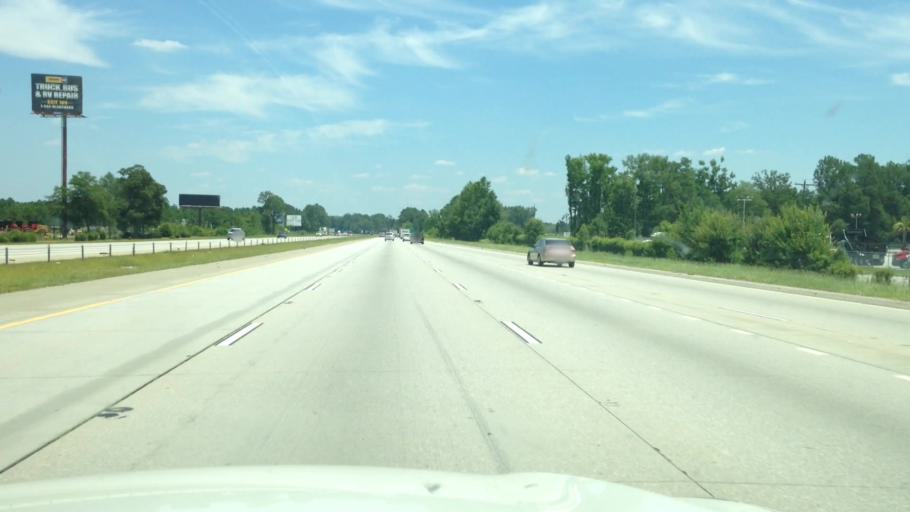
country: US
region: South Carolina
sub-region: Florence County
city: Florence
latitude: 34.2648
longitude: -79.7271
